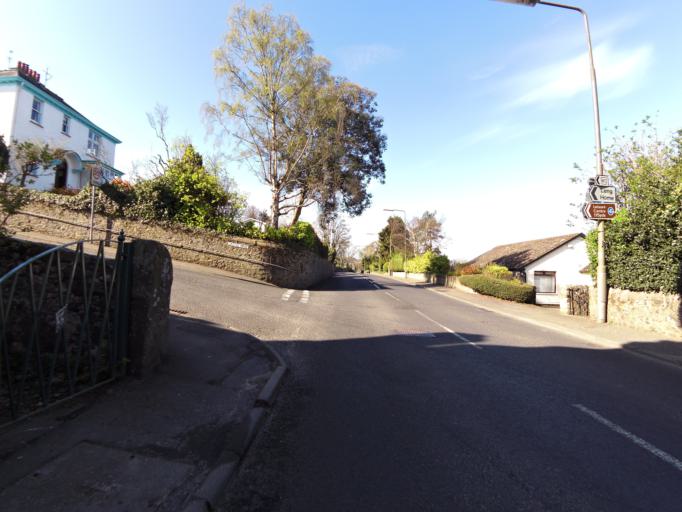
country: GB
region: Scotland
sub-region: Fife
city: Newport-On-Tay
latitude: 56.4335
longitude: -2.9538
